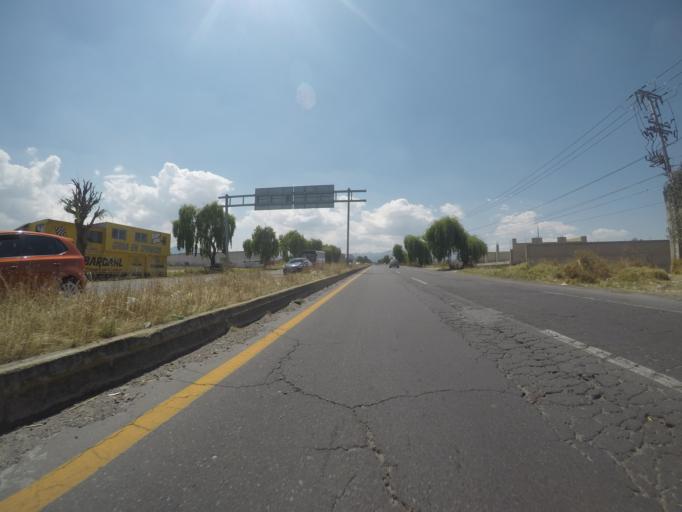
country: MX
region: Mexico
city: San Juan de las Huertas
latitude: 19.2520
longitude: -99.7474
